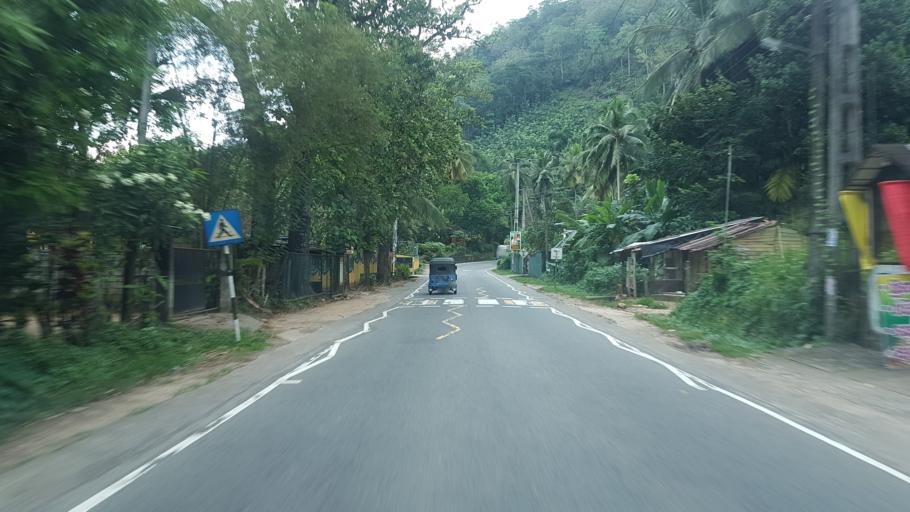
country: LK
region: Western
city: Hanwella Ihala
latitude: 7.0230
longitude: 80.2649
